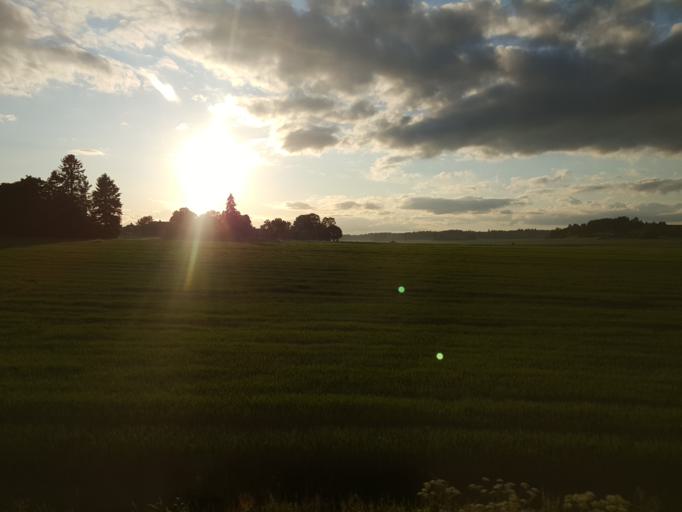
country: SE
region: Uppsala
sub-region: Uppsala Kommun
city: Vattholma
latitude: 59.9387
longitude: 17.8234
